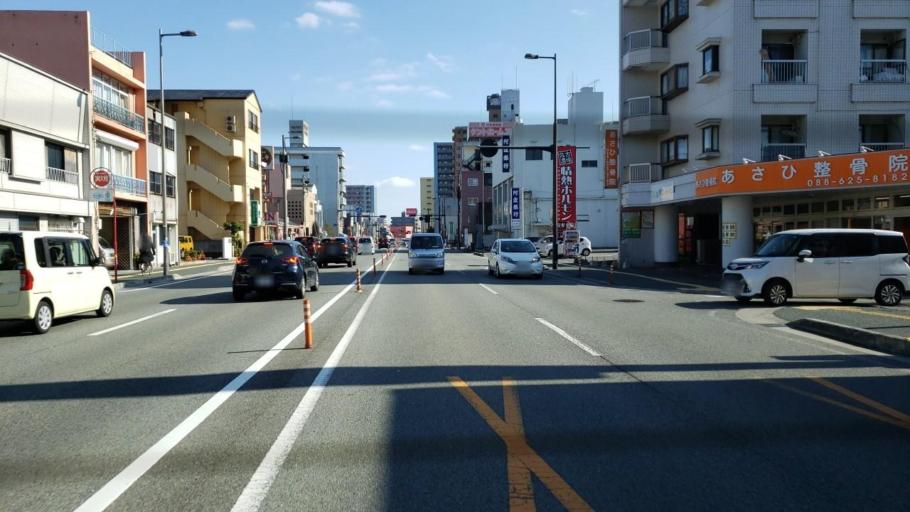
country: JP
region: Tokushima
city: Tokushima-shi
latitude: 34.0782
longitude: 134.5240
